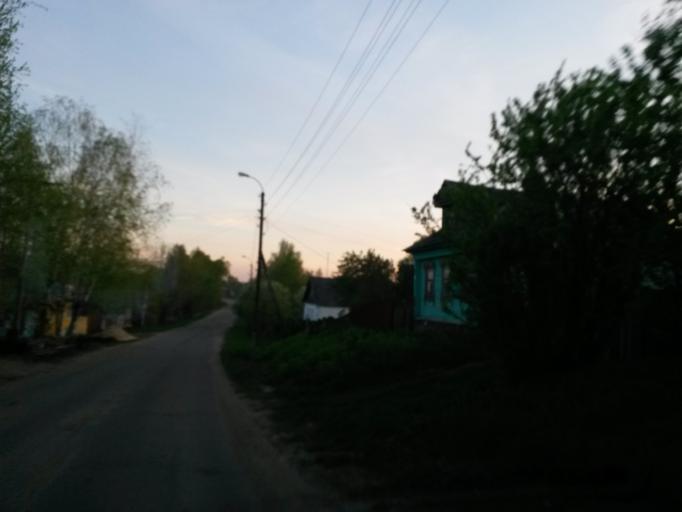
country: RU
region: Jaroslavl
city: Tutayev
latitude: 57.8896
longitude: 39.5557
